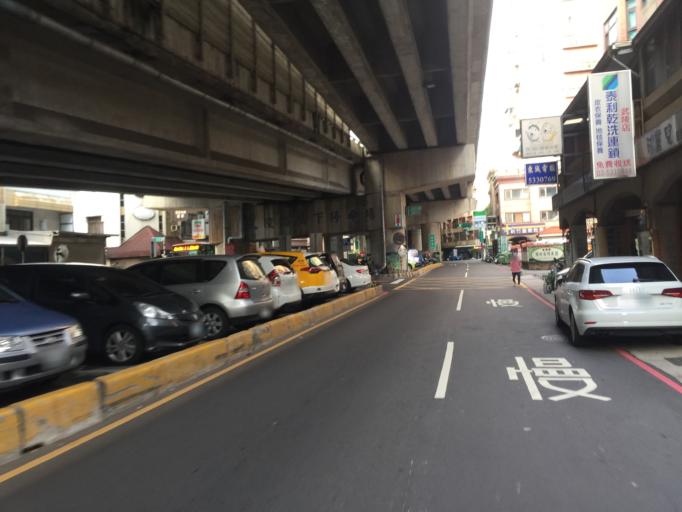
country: TW
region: Taiwan
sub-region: Hsinchu
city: Hsinchu
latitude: 24.8220
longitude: 120.9698
